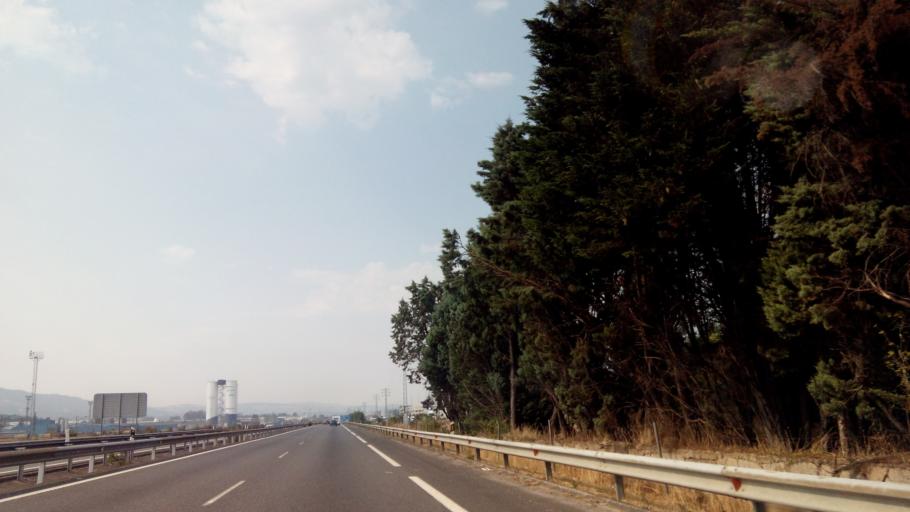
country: ES
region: Galicia
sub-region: Provincia de Pontevedra
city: Porrino
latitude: 42.1163
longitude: -8.6216
